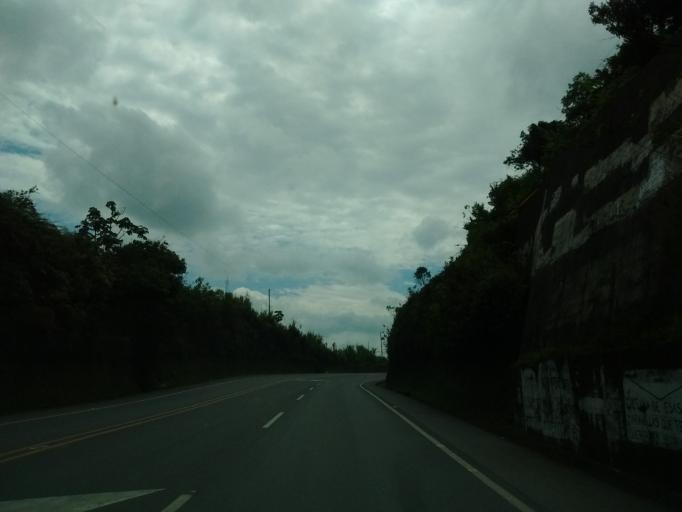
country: CO
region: Cauca
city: Cajibio
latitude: 2.5335
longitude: -76.5578
